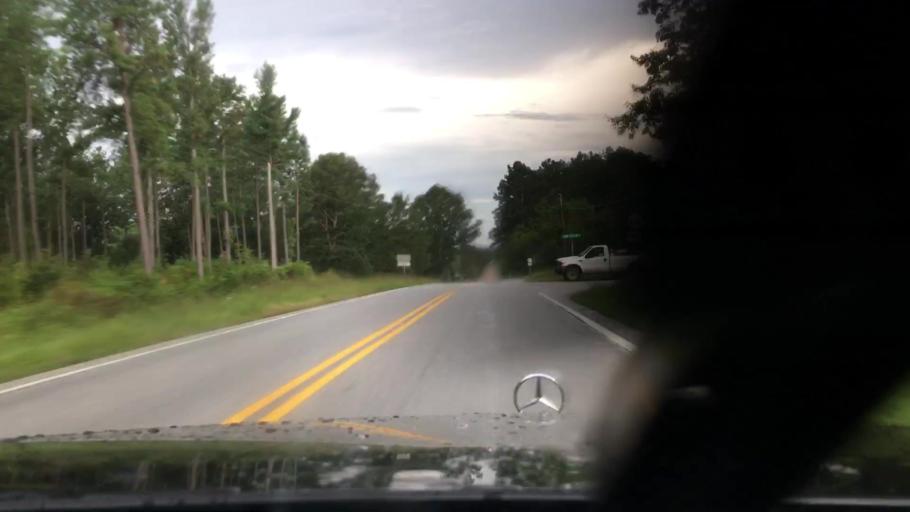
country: US
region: Virginia
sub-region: Nelson County
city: Lovingston
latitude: 37.7431
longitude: -78.9980
